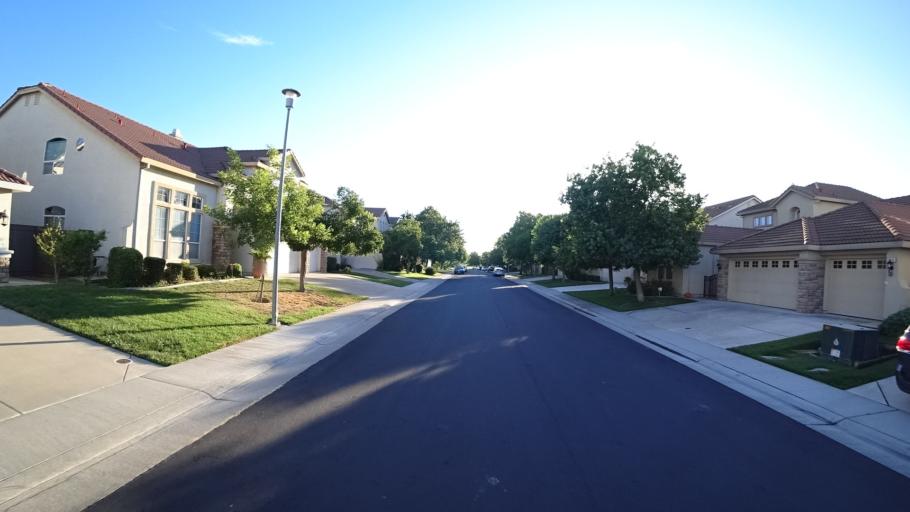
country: US
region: California
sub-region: Sacramento County
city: Laguna
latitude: 38.3954
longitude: -121.4766
